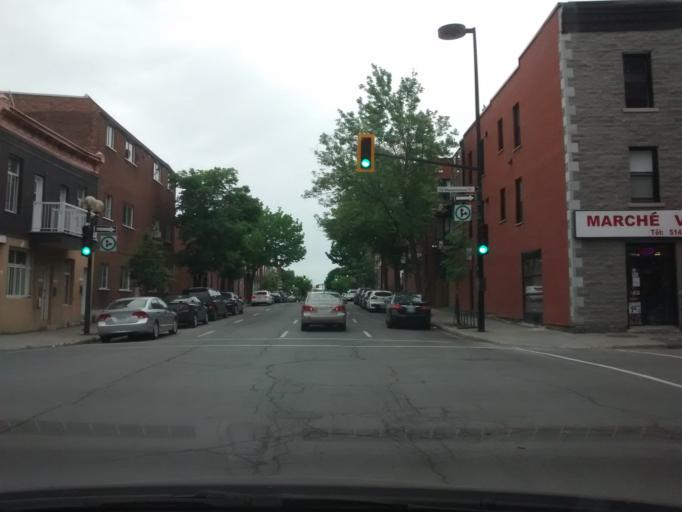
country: CA
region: Quebec
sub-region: Monteregie
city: Longueuil
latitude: 45.5301
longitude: -73.5479
